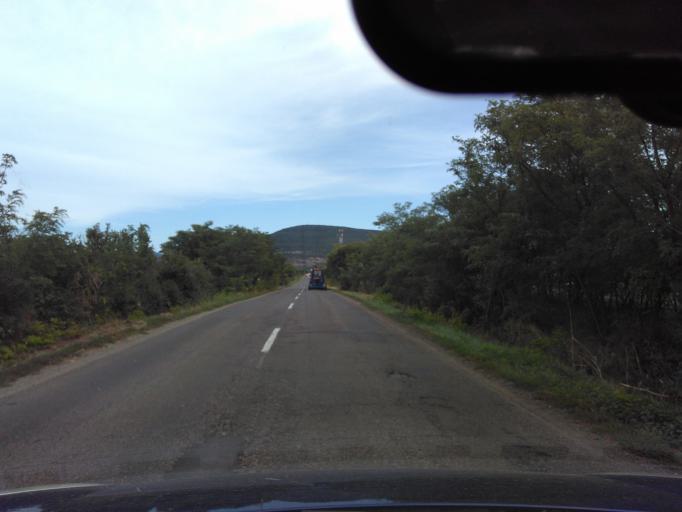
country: HU
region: Nograd
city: Jobbagyi
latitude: 47.8289
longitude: 19.6559
